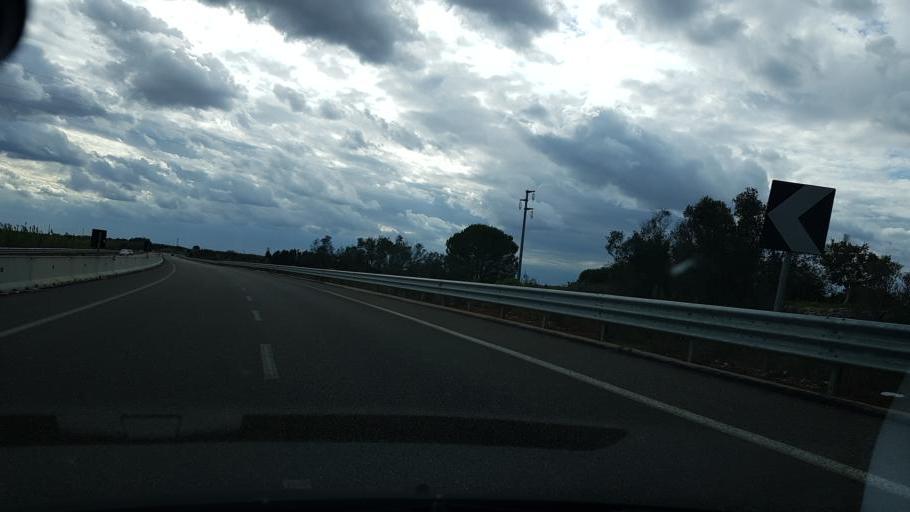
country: IT
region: Apulia
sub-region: Provincia di Lecce
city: Palmariggi
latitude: 40.1324
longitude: 18.3913
